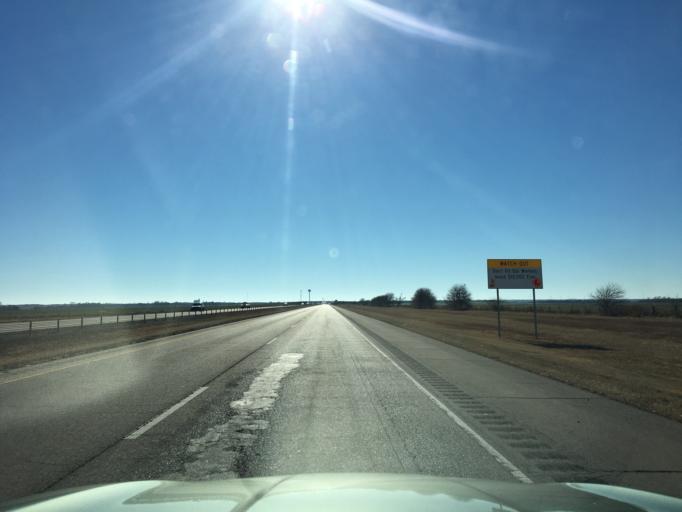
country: US
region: Oklahoma
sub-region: Kay County
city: Blackwell
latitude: 36.9660
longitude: -97.3458
